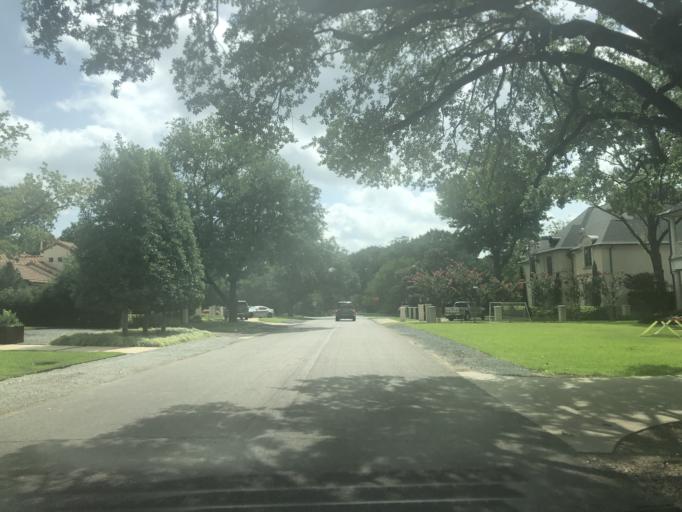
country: US
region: Texas
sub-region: Dallas County
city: University Park
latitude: 32.8676
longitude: -96.8351
